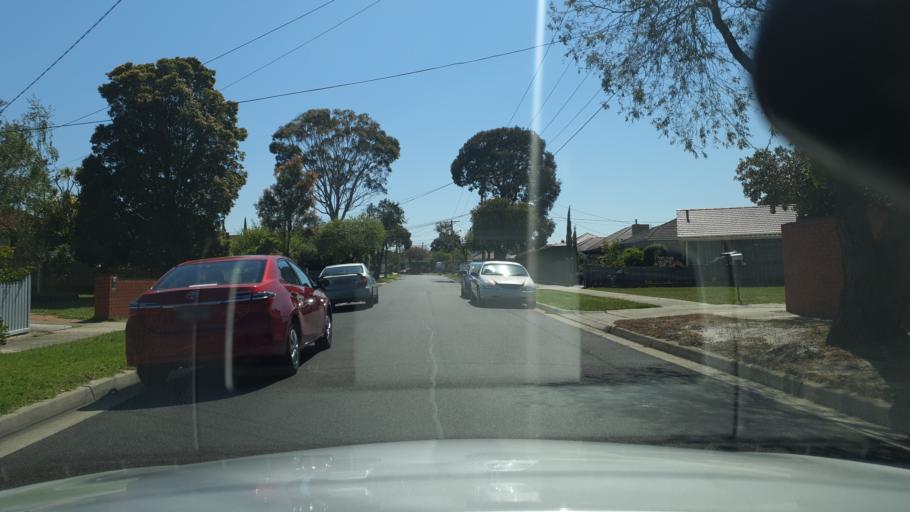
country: AU
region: Victoria
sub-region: Greater Dandenong
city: Noble Park North
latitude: -37.9334
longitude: 145.1742
